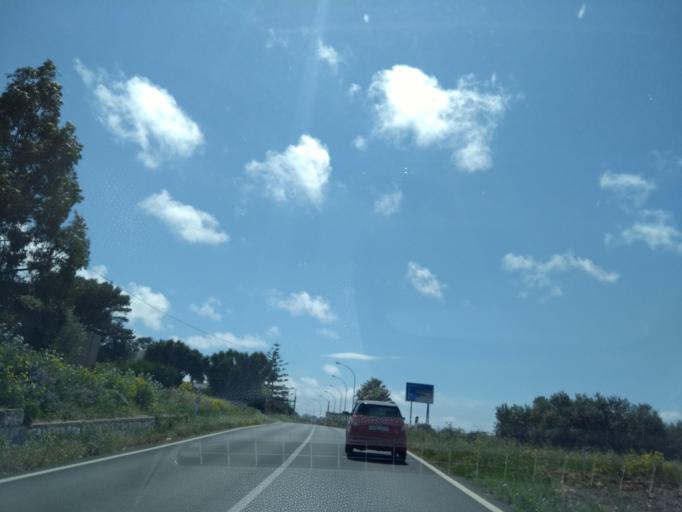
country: IT
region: Sicily
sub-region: Trapani
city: Marsala
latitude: 37.8744
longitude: 12.5207
